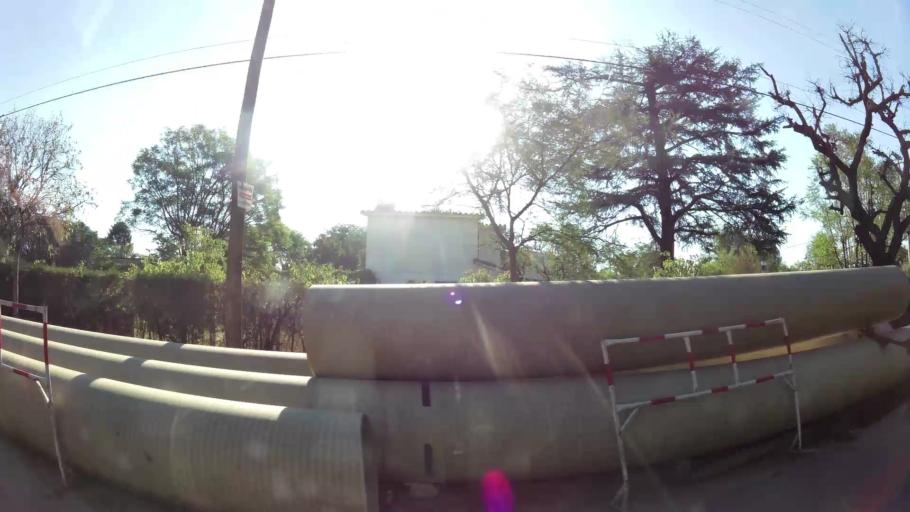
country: AR
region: Cordoba
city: Villa Allende
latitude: -31.3538
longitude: -64.2516
